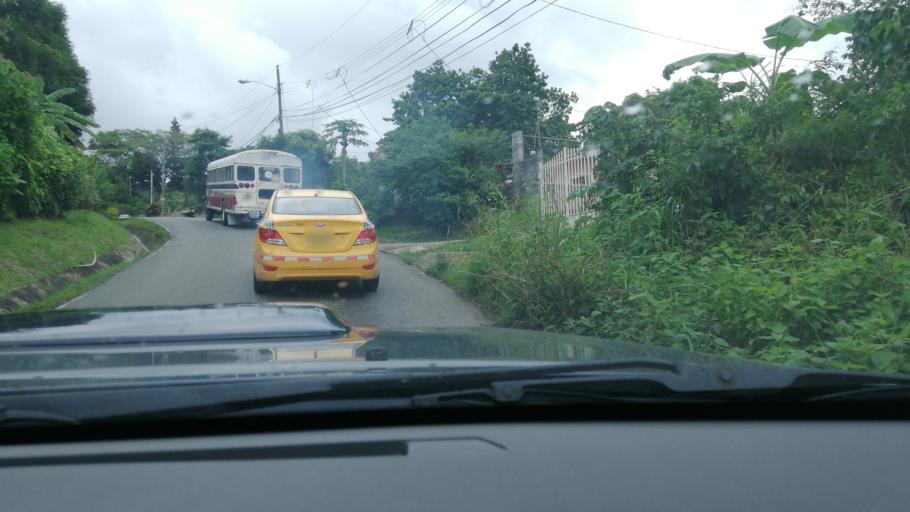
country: PA
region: Panama
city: San Miguelito
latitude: 9.0970
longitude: -79.4482
